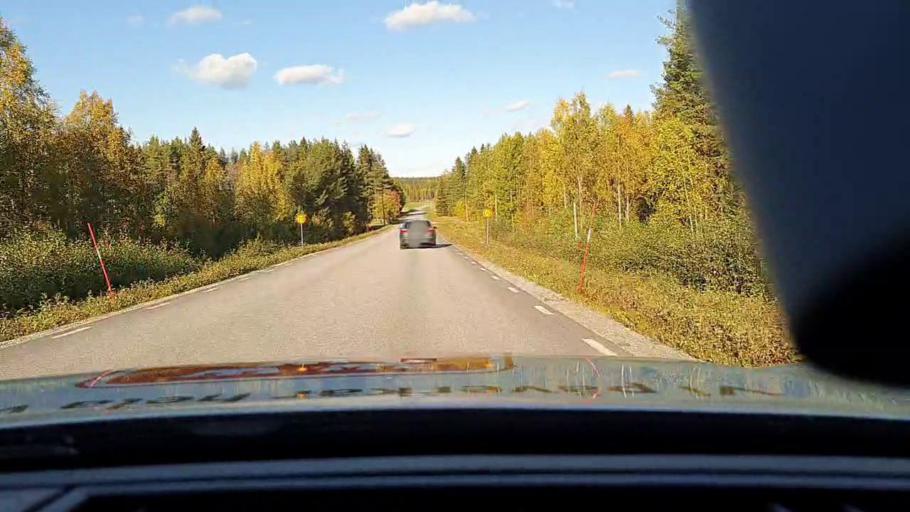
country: SE
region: Norrbotten
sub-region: Pitea Kommun
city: Norrfjarden
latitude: 65.5077
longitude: 21.4843
